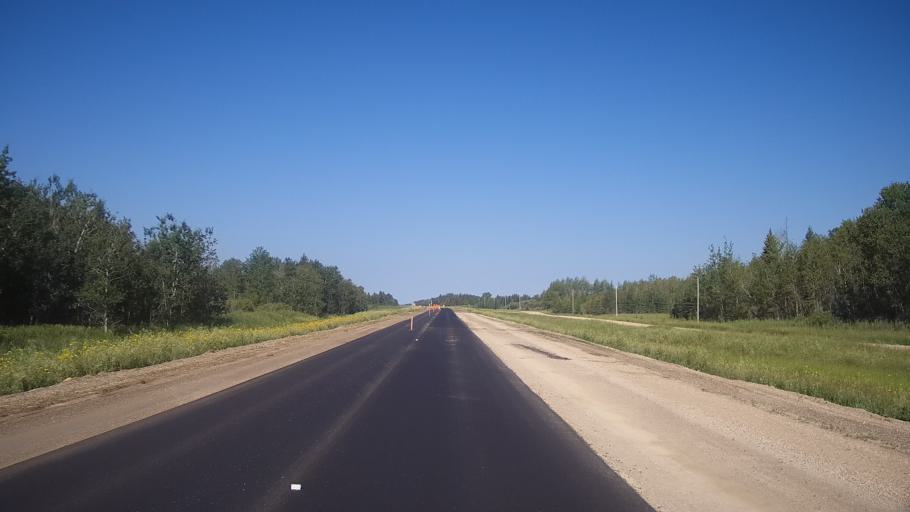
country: CA
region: Manitoba
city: Lac du Bonnet
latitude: 49.6500
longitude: -95.8300
